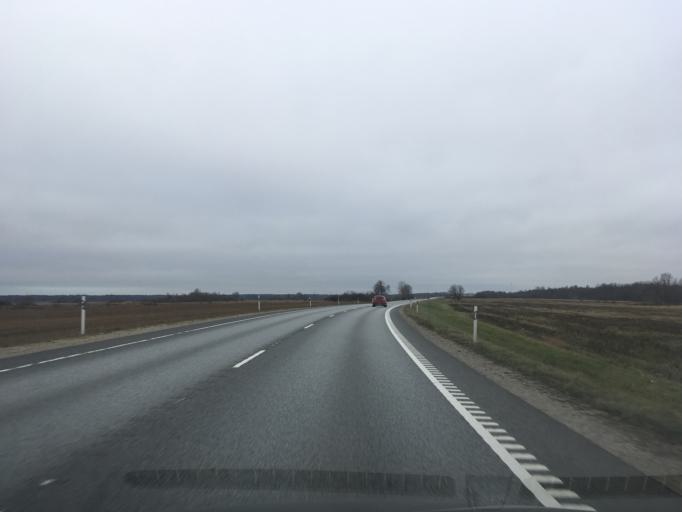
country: EE
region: Ida-Virumaa
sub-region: Narva-Joesuu linn
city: Narva-Joesuu
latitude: 59.4018
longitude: 28.0147
